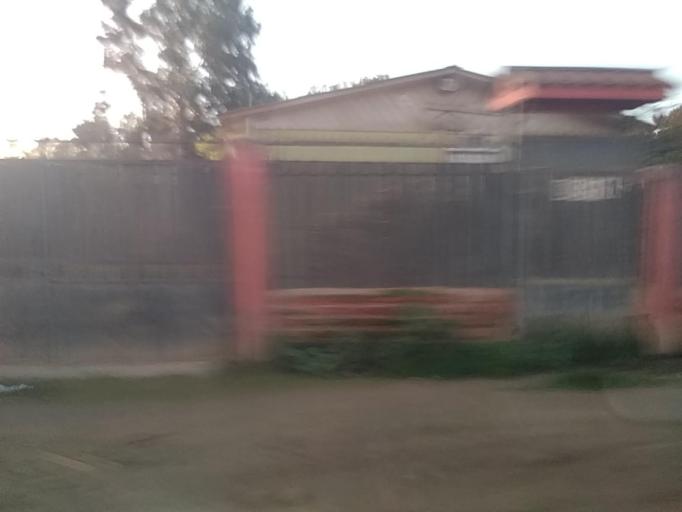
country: CL
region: Valparaiso
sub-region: San Antonio Province
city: El Tabo
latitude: -33.4544
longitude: -71.6586
